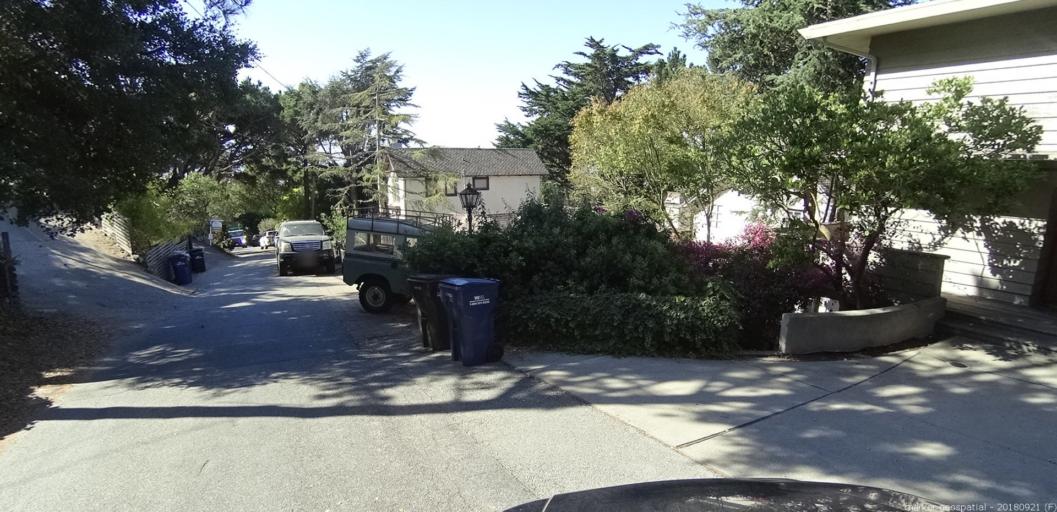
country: US
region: California
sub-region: Monterey County
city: Carmel-by-the-Sea
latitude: 36.5643
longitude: -121.9147
